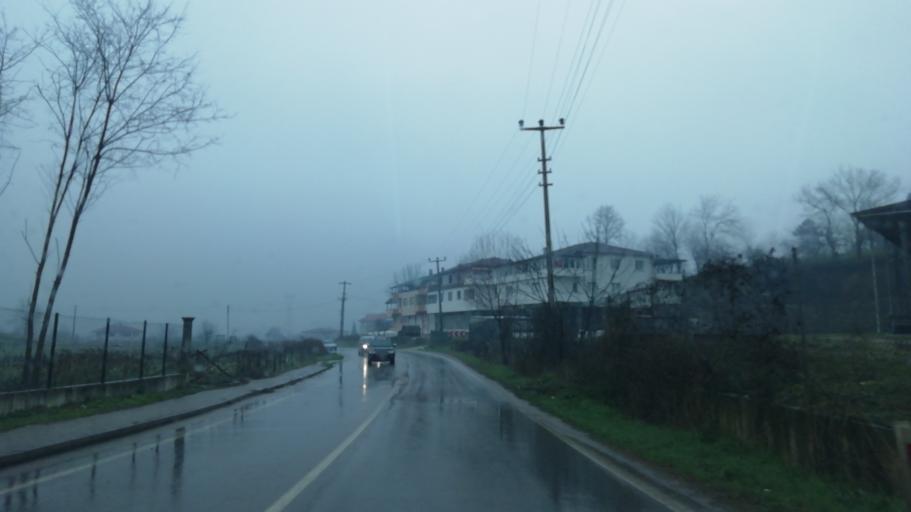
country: TR
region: Sakarya
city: Karapurcek
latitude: 40.6897
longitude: 30.4945
